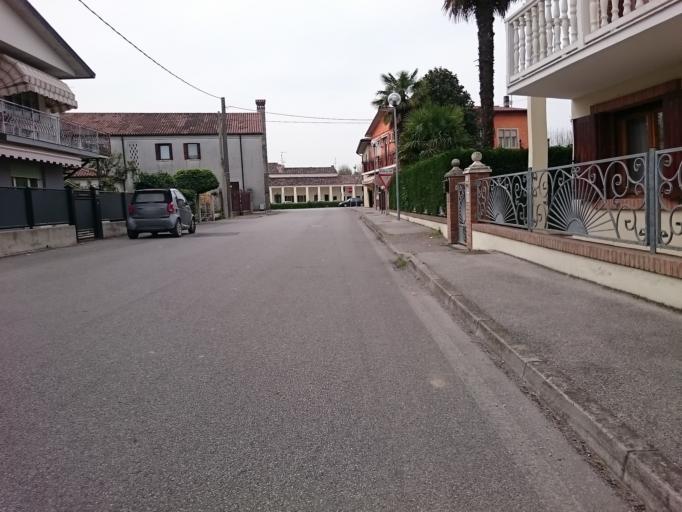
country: IT
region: Veneto
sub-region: Provincia di Padova
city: Bagnoli di Sopra
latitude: 45.1859
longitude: 11.8814
